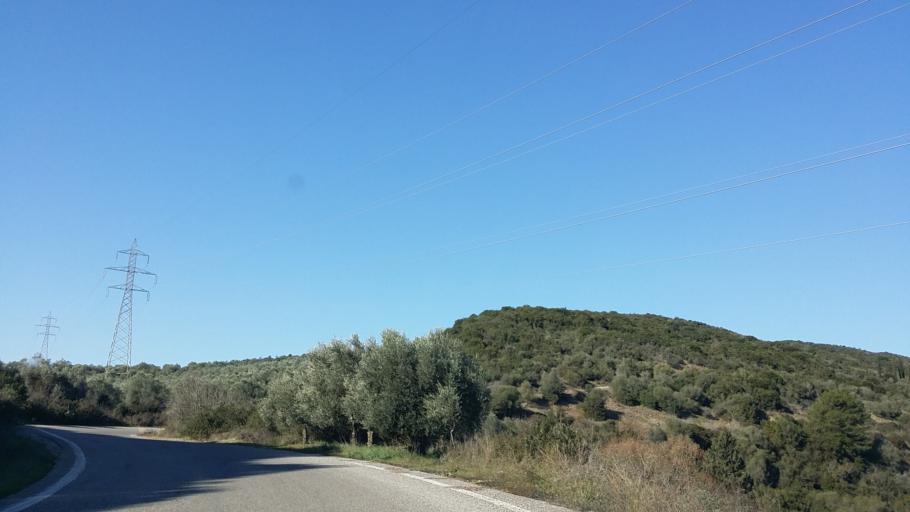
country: GR
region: West Greece
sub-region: Nomos Aitolias kai Akarnanias
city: Lepenou
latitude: 38.7444
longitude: 21.3454
